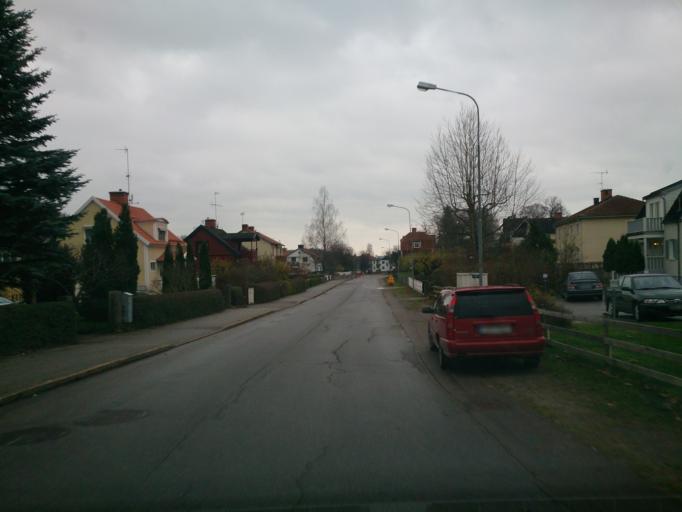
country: SE
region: OEstergoetland
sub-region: Atvidabergs Kommun
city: Atvidaberg
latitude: 58.2056
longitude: 15.9918
